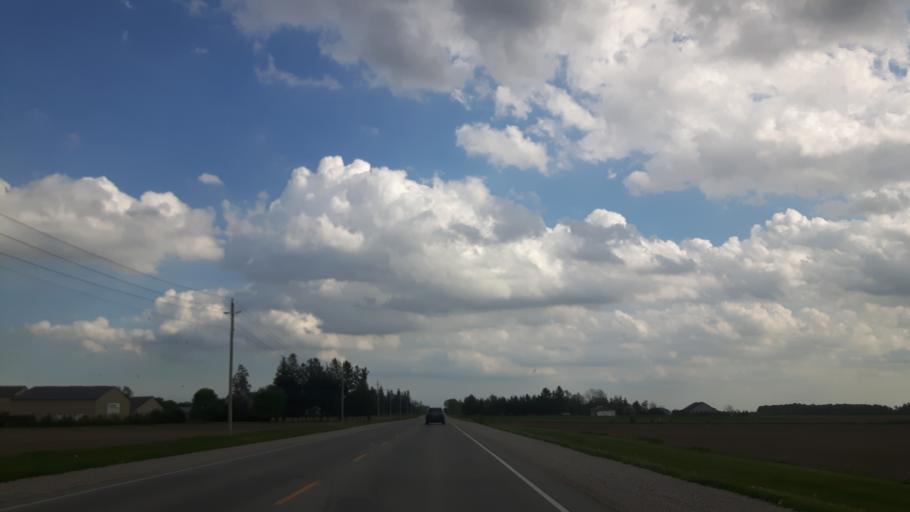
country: CA
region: Ontario
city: South Huron
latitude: 43.3950
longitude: -81.4905
